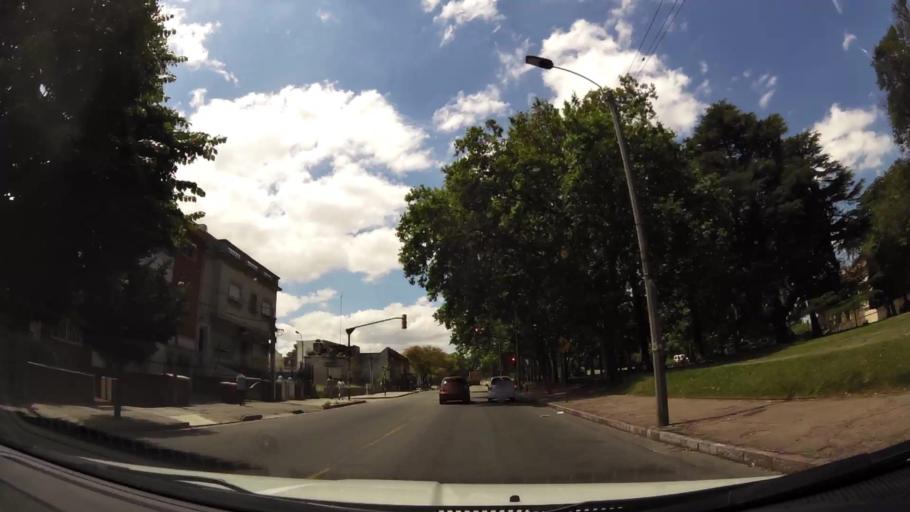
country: UY
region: Montevideo
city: Montevideo
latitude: -34.8588
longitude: -56.2131
